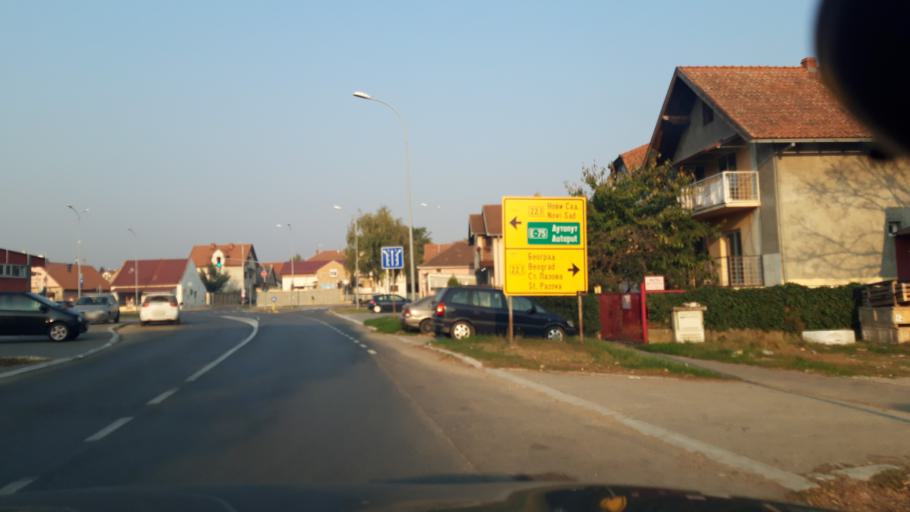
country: RS
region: Autonomna Pokrajina Vojvodina
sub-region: Sremski Okrug
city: Ingija
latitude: 45.0403
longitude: 20.0872
